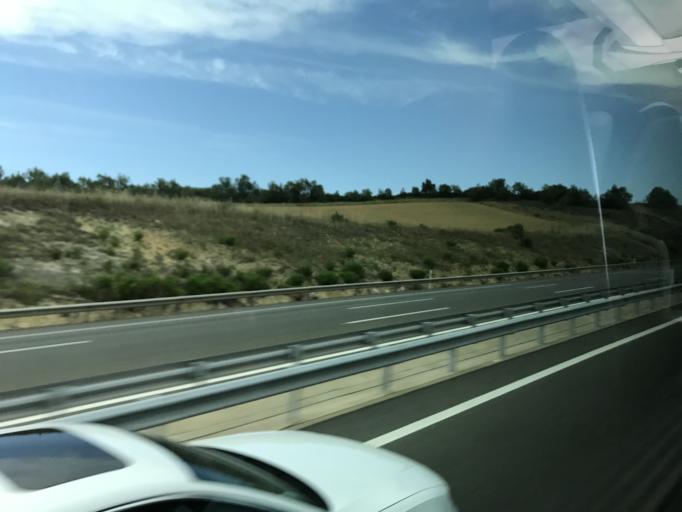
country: ES
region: Basque Country
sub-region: Provincia de Alava
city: Arminon
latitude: 42.7065
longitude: -2.9003
